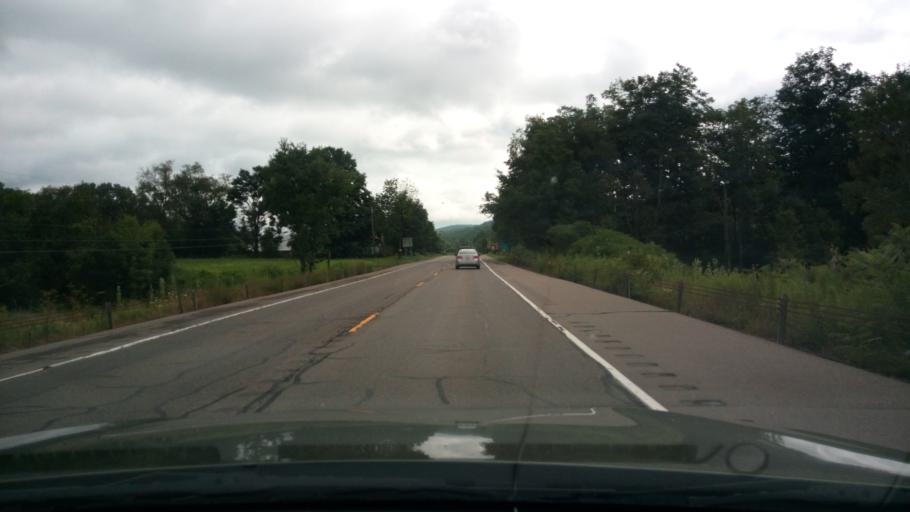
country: US
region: New York
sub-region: Chemung County
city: Horseheads North
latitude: 42.2954
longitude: -76.6924
